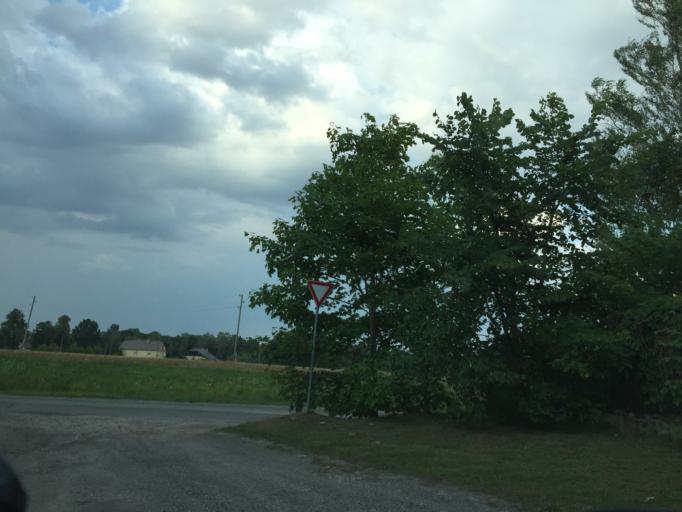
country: LV
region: Dobeles Rajons
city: Dobele
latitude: 56.6021
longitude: 23.3042
